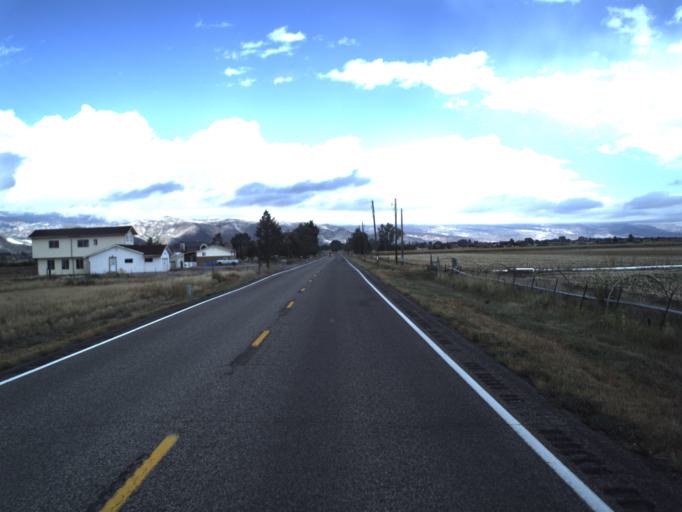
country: US
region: Utah
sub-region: Sevier County
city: Monroe
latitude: 38.6545
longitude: -112.1215
